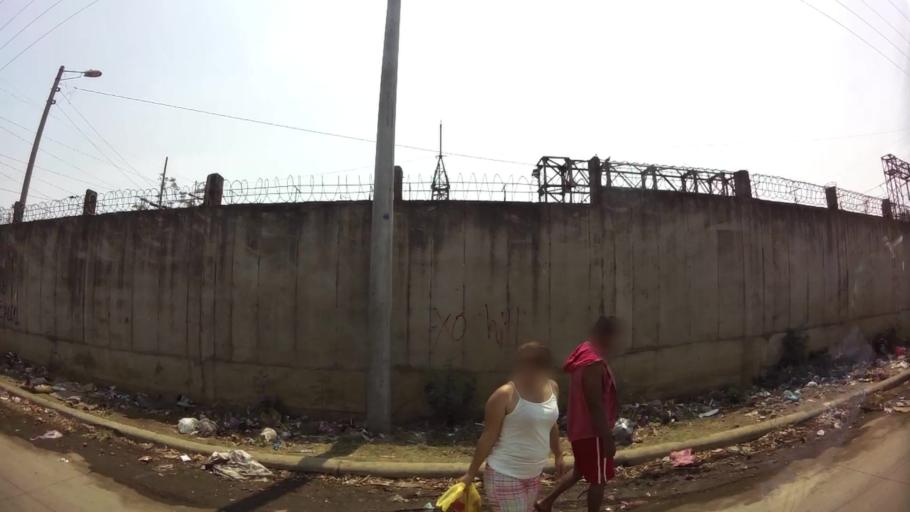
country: NI
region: Managua
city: Ciudad Sandino
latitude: 12.1587
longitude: -86.3121
